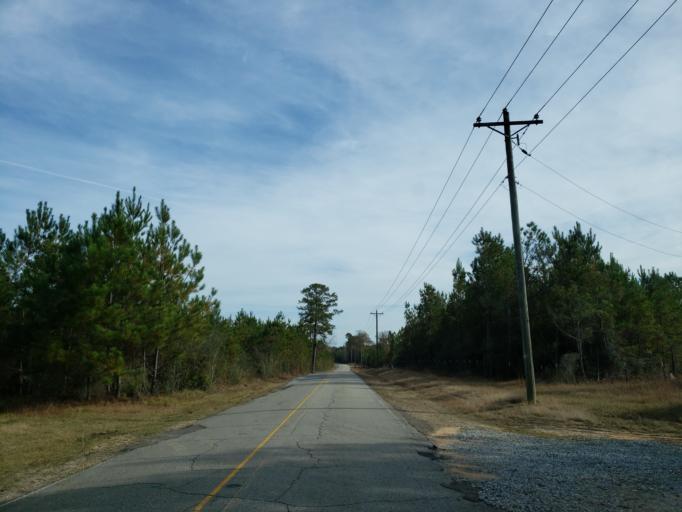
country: US
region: Mississippi
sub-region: Forrest County
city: Rawls Springs
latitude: 31.4185
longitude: -89.4232
